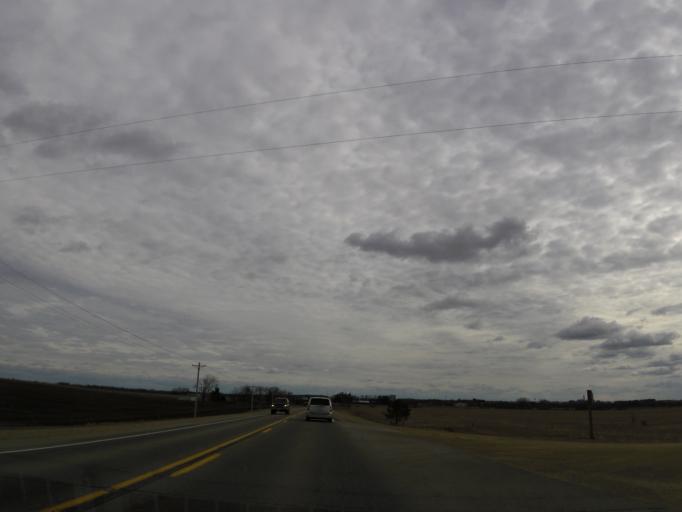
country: US
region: Iowa
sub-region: Chickasaw County
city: New Hampton
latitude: 43.1057
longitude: -92.2979
